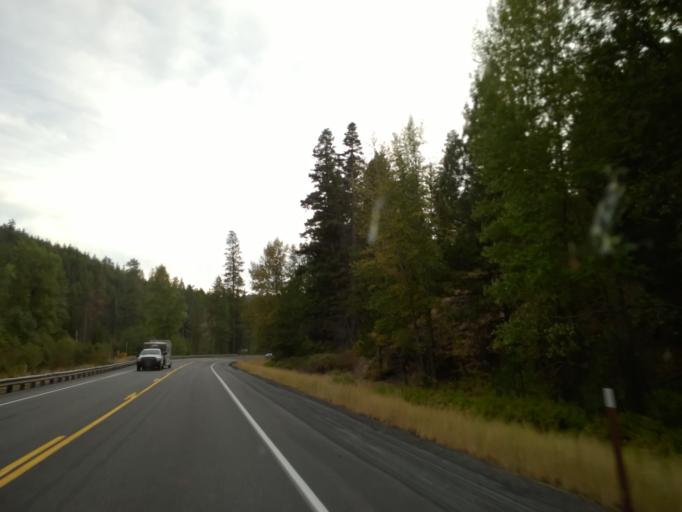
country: US
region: Washington
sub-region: Kittitas County
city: Cle Elum
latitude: 47.3048
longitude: -120.6956
